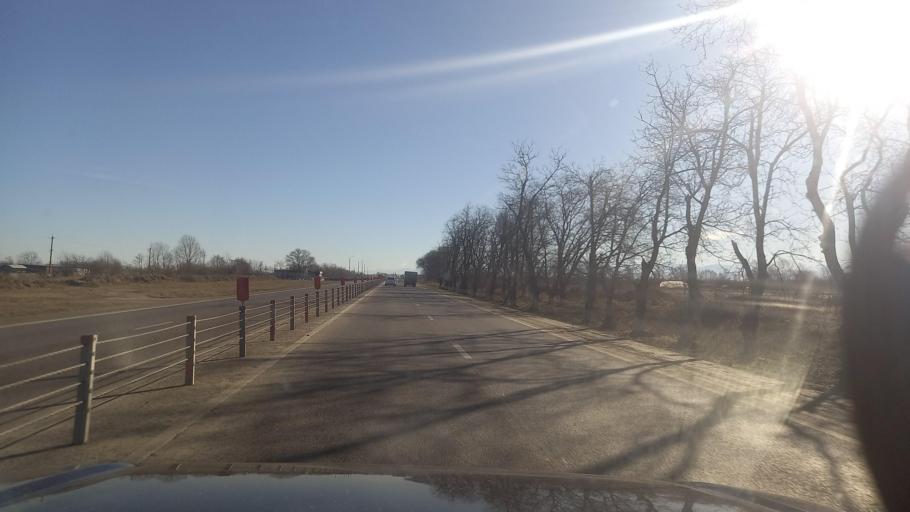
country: RU
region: Kabardino-Balkariya
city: Staryy Cherek
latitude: 43.4836
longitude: 43.8111
